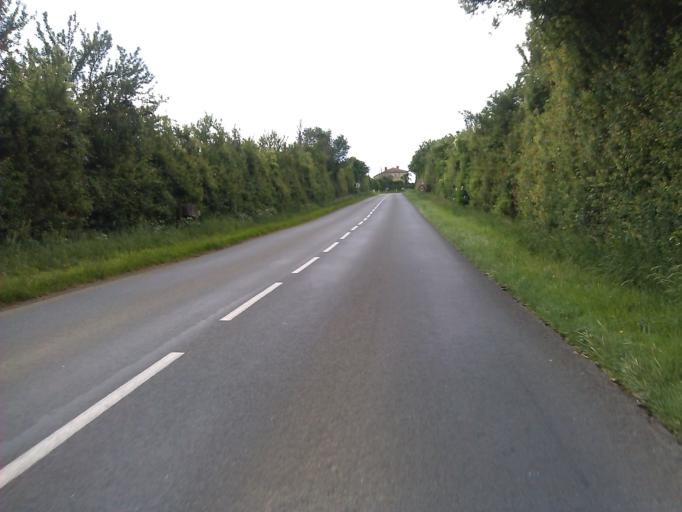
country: FR
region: Poitou-Charentes
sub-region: Departement de la Charente
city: Nanteuil-en-Vallee
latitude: 45.9848
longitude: 0.3646
